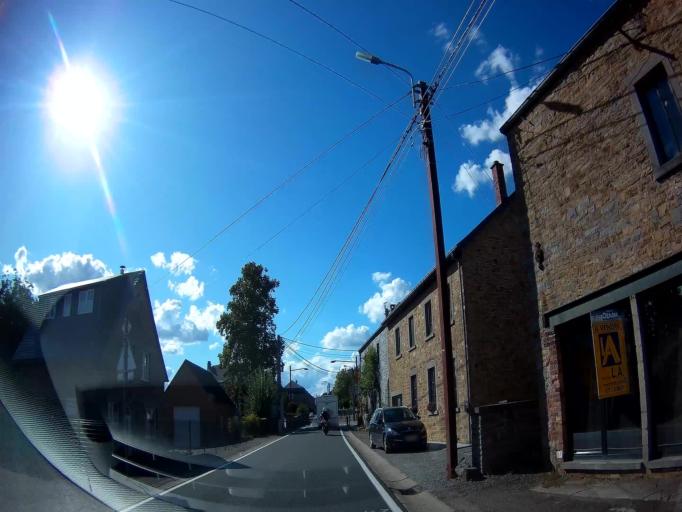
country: BE
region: Wallonia
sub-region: Province de Namur
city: Mettet
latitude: 50.3180
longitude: 4.7530
